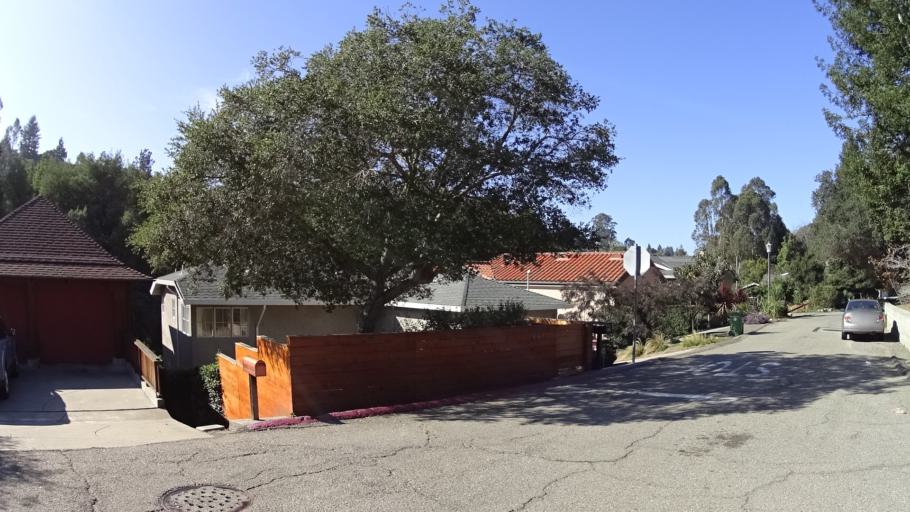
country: US
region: California
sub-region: Alameda County
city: Piedmont
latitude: 37.8427
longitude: -122.2241
